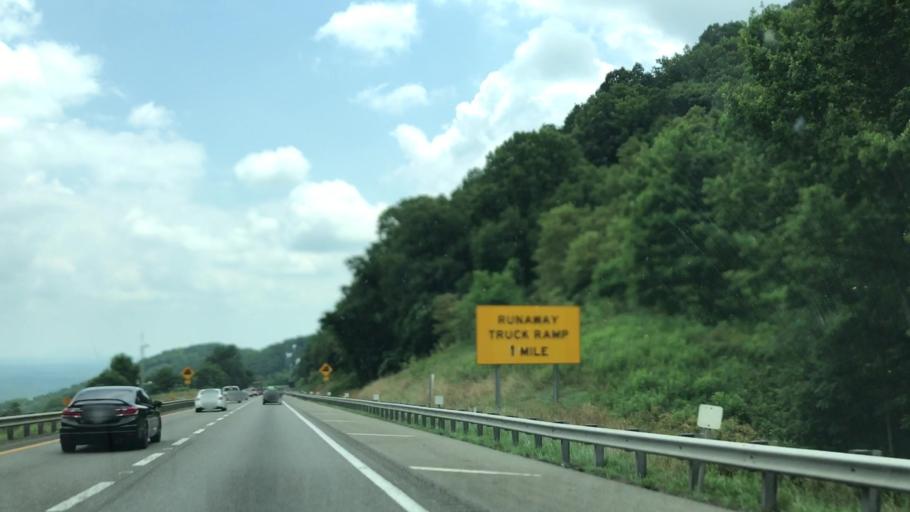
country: US
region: Virginia
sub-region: Carroll County
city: Cana
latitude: 36.6111
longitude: -80.7394
